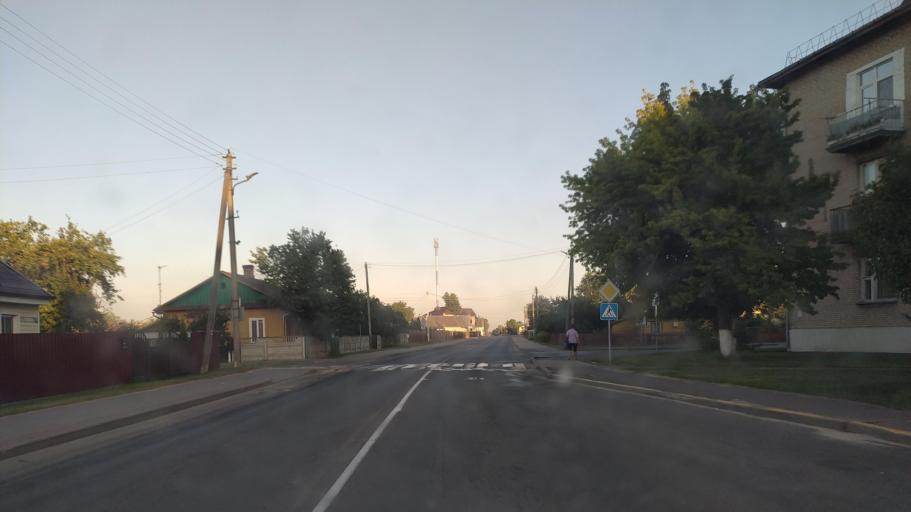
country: BY
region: Brest
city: Byaroza
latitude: 52.5394
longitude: 24.9820
